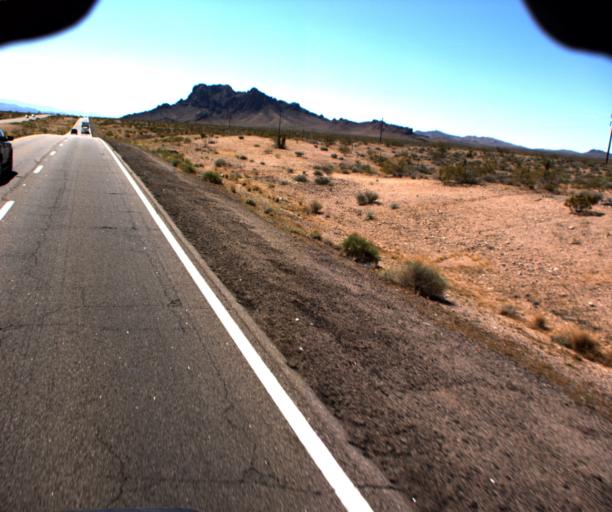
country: US
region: Nevada
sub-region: Clark County
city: Boulder City
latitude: 35.8136
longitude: -114.5471
